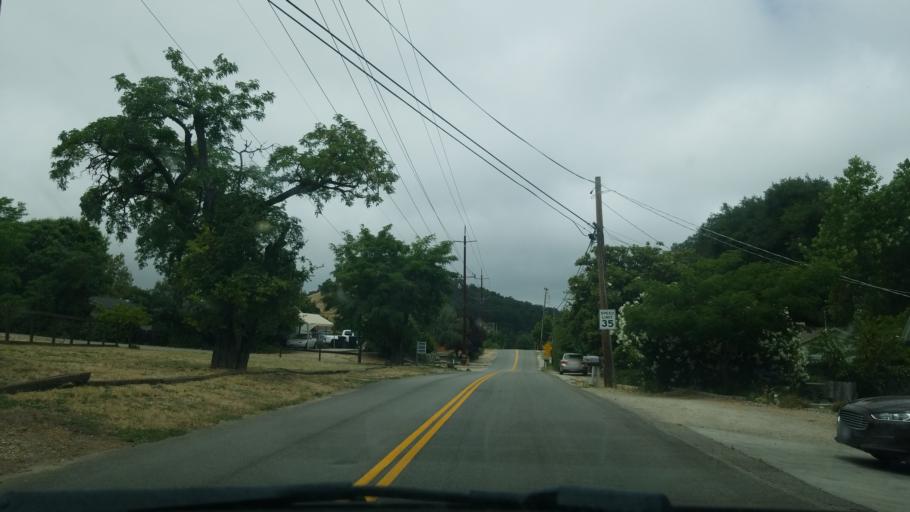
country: US
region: California
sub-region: San Luis Obispo County
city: Atascadero
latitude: 35.4635
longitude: -120.6688
